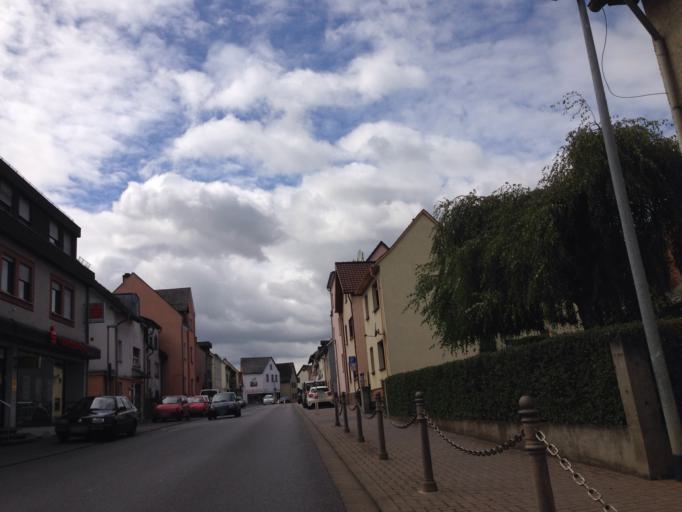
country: DE
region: Hesse
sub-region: Regierungsbezirk Giessen
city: Limburg an der Lahn
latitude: 50.3972
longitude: 8.0417
